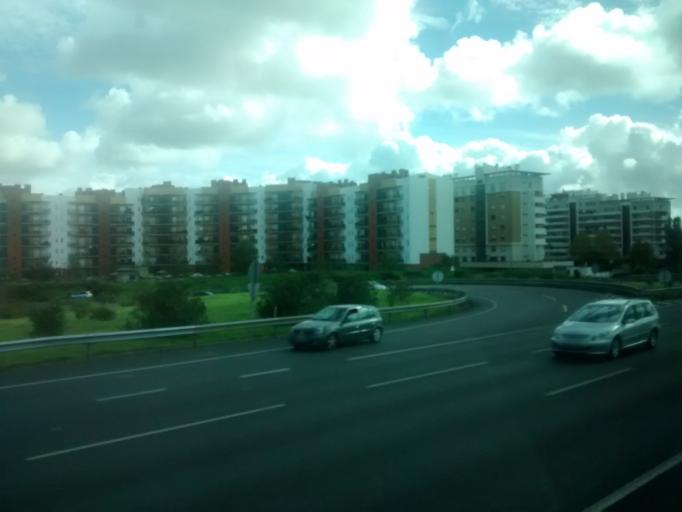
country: PT
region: Lisbon
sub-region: Odivelas
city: Pontinha
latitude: 38.7571
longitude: -9.1721
